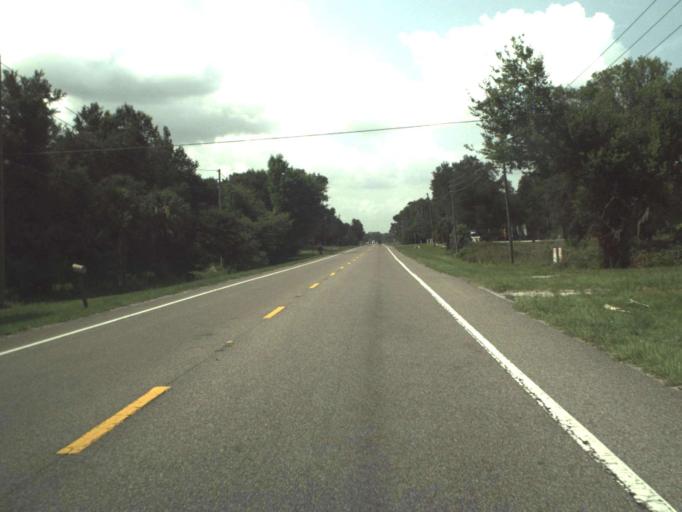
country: US
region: Florida
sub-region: Sumter County
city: Wildwood
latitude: 28.8183
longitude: -82.0456
